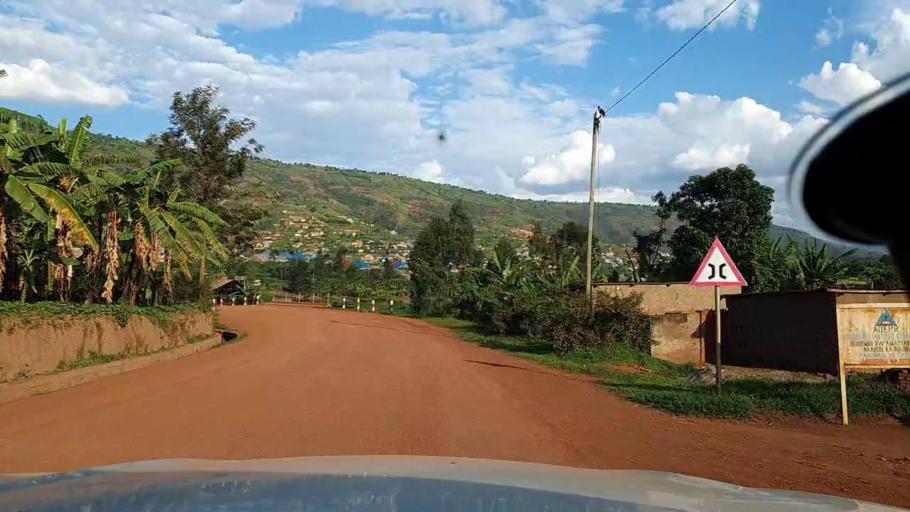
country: RW
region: Kigali
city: Kigali
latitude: -1.9026
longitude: 29.9723
